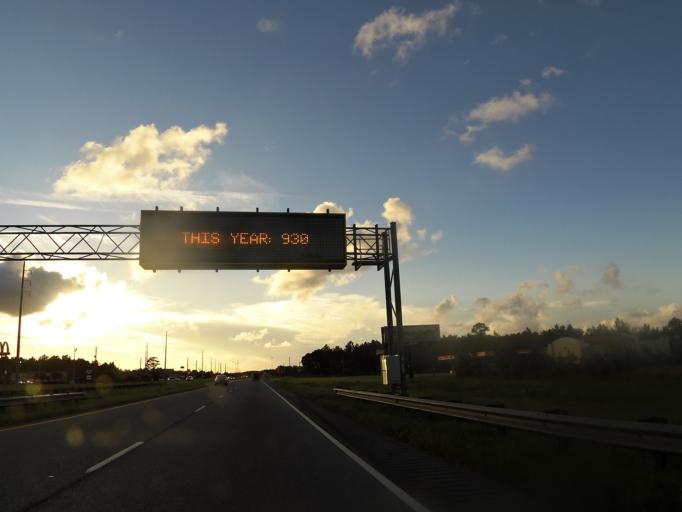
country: US
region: Georgia
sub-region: Glynn County
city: Brunswick
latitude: 31.1340
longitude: -81.5657
